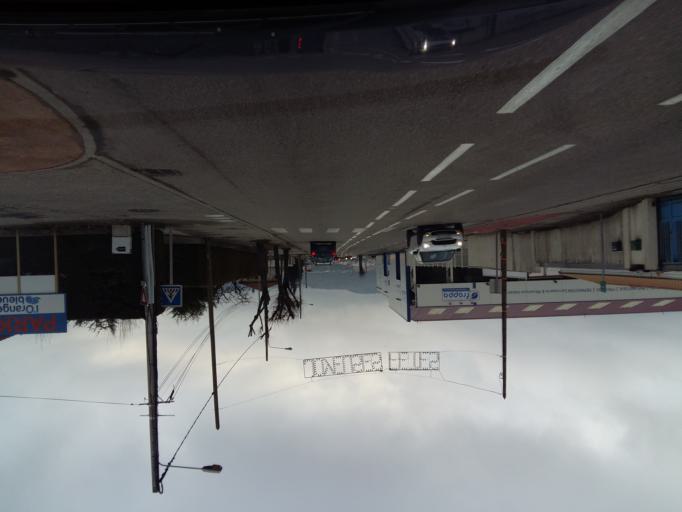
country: FR
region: Rhone-Alpes
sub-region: Departement de l'Ardeche
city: Davezieux
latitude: 45.2556
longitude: 4.7001
